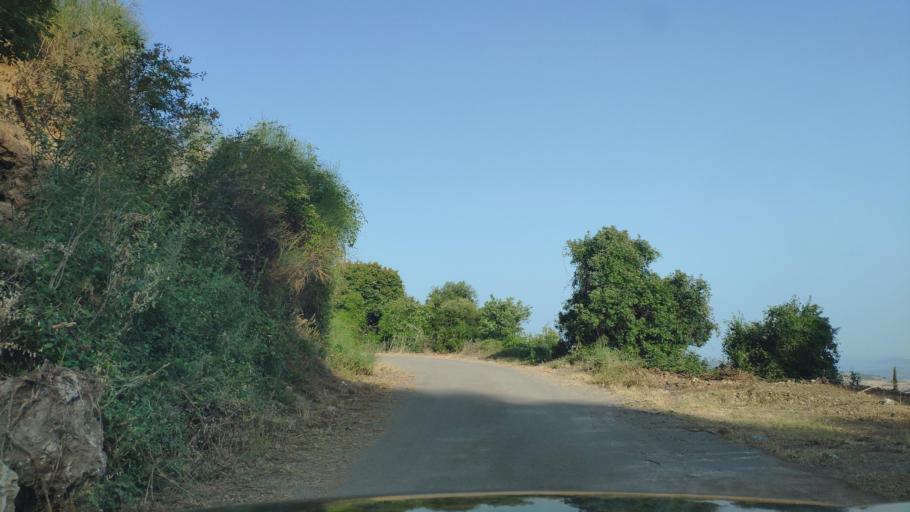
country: GR
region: West Greece
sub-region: Nomos Aitolias kai Akarnanias
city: Monastirakion
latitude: 38.8524
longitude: 20.9814
